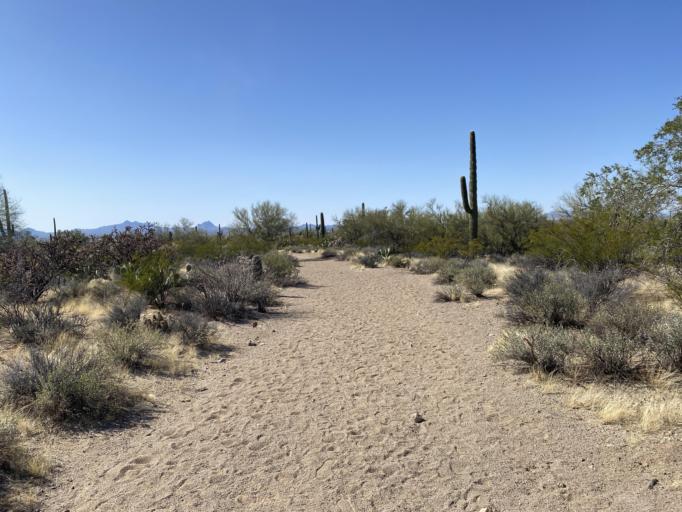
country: US
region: Arizona
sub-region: Pima County
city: Picture Rocks
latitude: 32.3038
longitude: -111.2108
